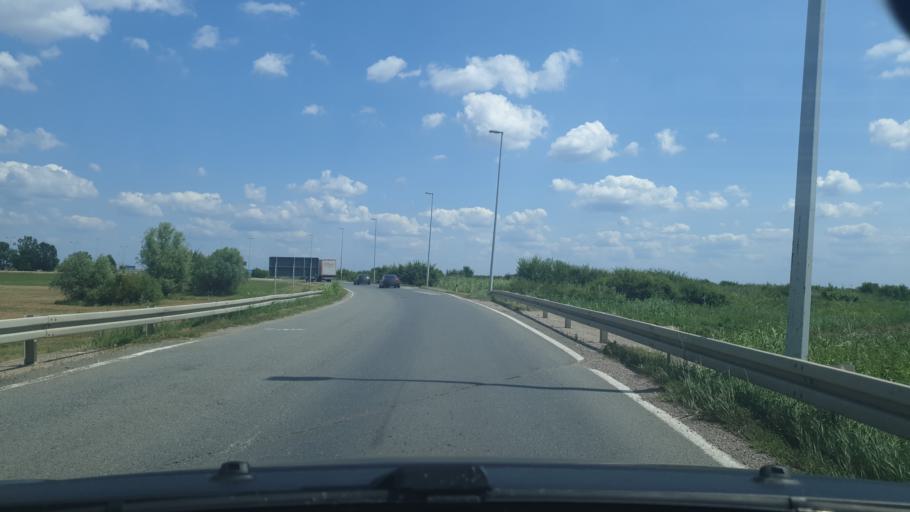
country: RS
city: Simanovci
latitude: 44.8757
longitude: 20.1221
